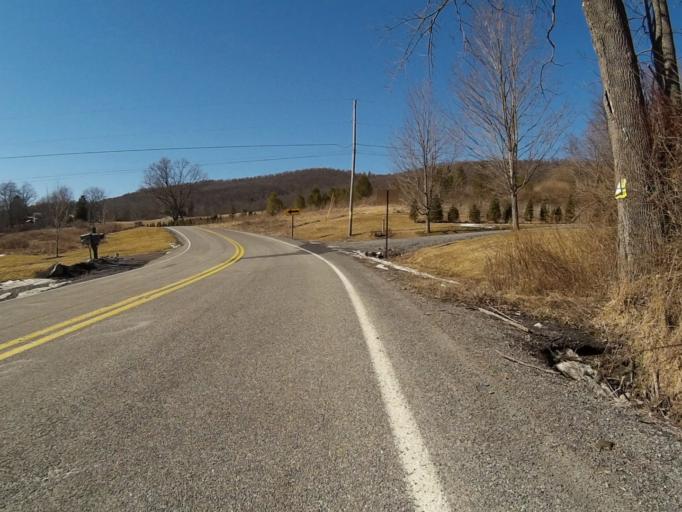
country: US
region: Pennsylvania
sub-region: Centre County
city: Park Forest Village
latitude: 40.8352
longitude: -77.9382
